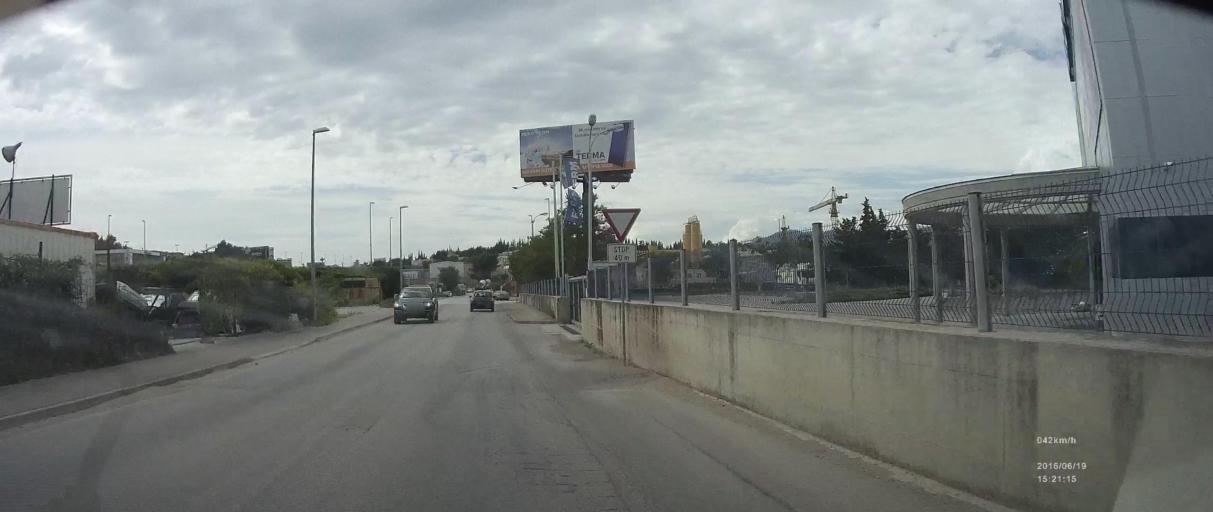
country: HR
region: Splitsko-Dalmatinska
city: Kamen
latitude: 43.5081
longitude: 16.5031
